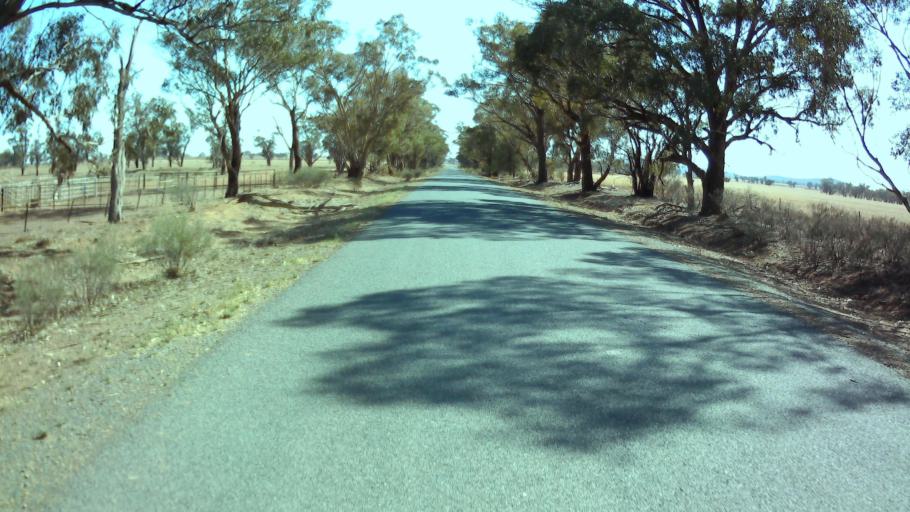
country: AU
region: New South Wales
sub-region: Weddin
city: Grenfell
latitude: -33.7424
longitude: 147.8802
